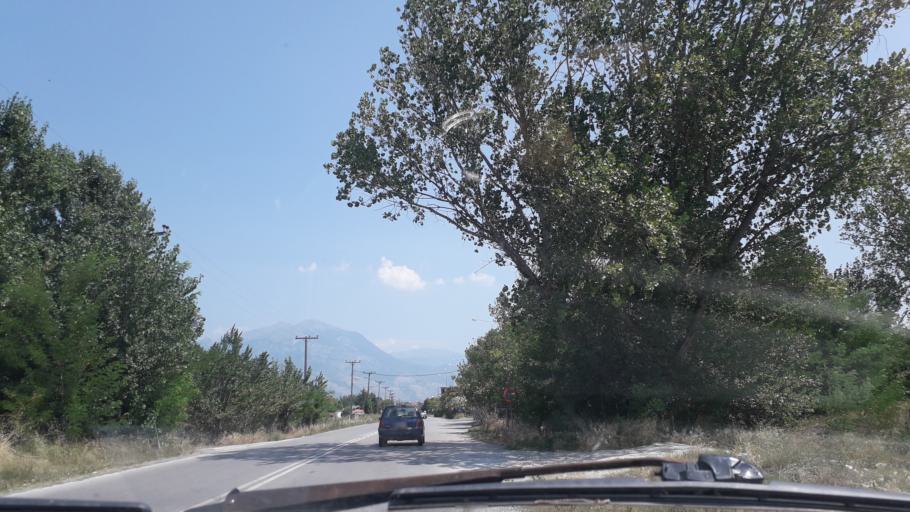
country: GR
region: Central Macedonia
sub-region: Nomos Pellis
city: Aridaia
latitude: 40.9640
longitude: 22.0518
